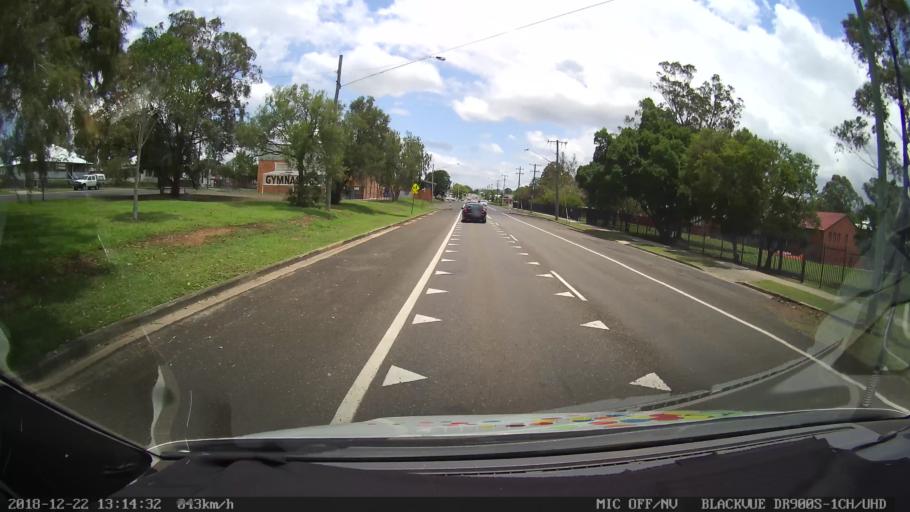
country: AU
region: New South Wales
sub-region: Clarence Valley
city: South Grafton
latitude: -29.7115
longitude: 152.9409
